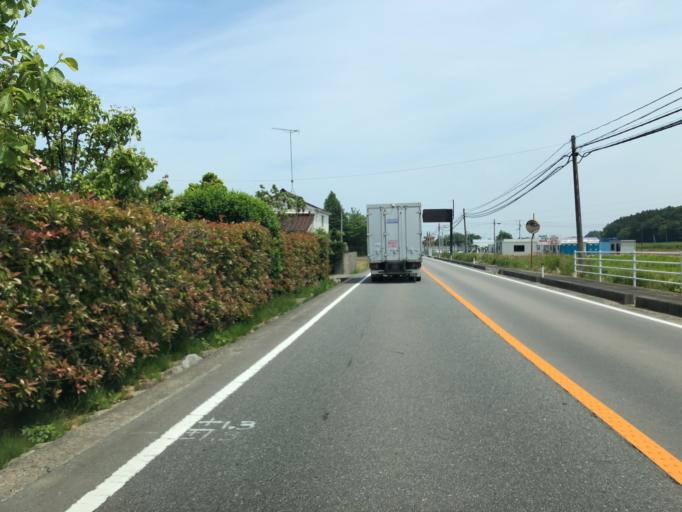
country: JP
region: Fukushima
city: Namie
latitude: 37.4986
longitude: 140.9611
